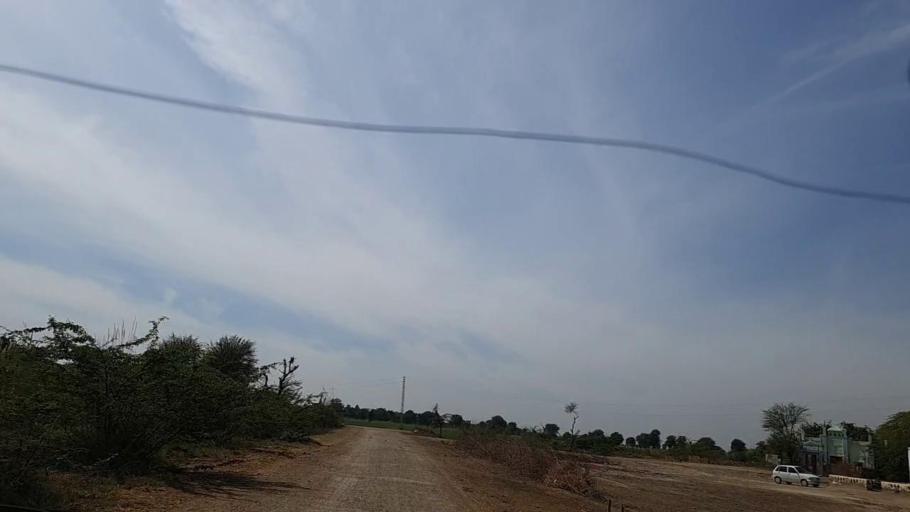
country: PK
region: Sindh
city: Dhoro Naro
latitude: 25.4928
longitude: 69.4925
